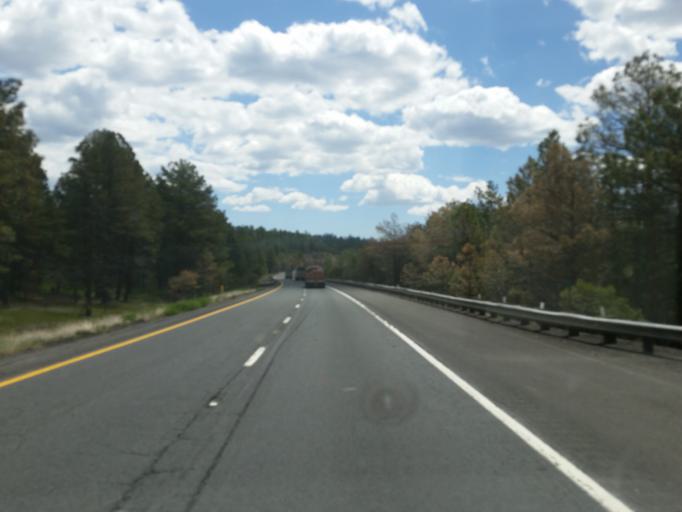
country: US
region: Arizona
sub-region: Coconino County
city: Parks
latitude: 35.2525
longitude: -111.9085
